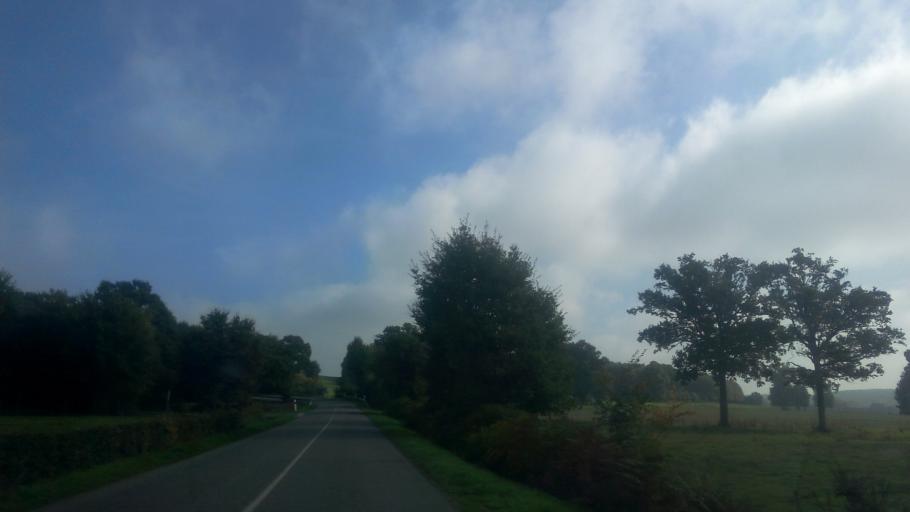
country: FR
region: Pays de la Loire
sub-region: Departement de la Loire-Atlantique
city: Conquereuil
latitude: 47.6252
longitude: -1.7673
